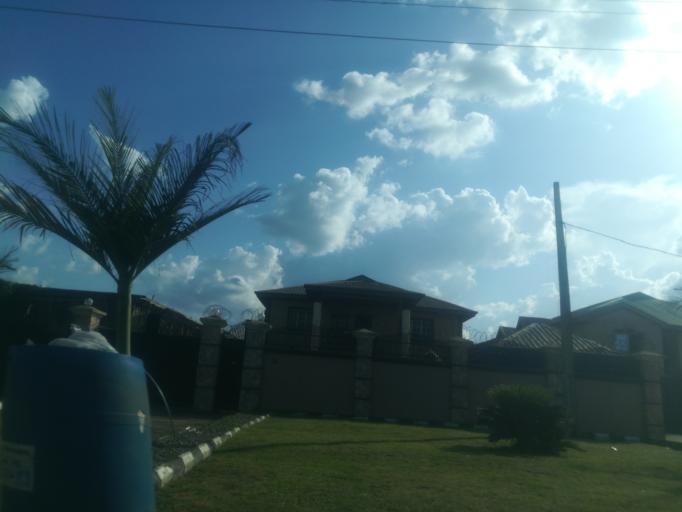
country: NG
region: Oyo
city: Ibadan
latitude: 7.4377
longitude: 3.9685
